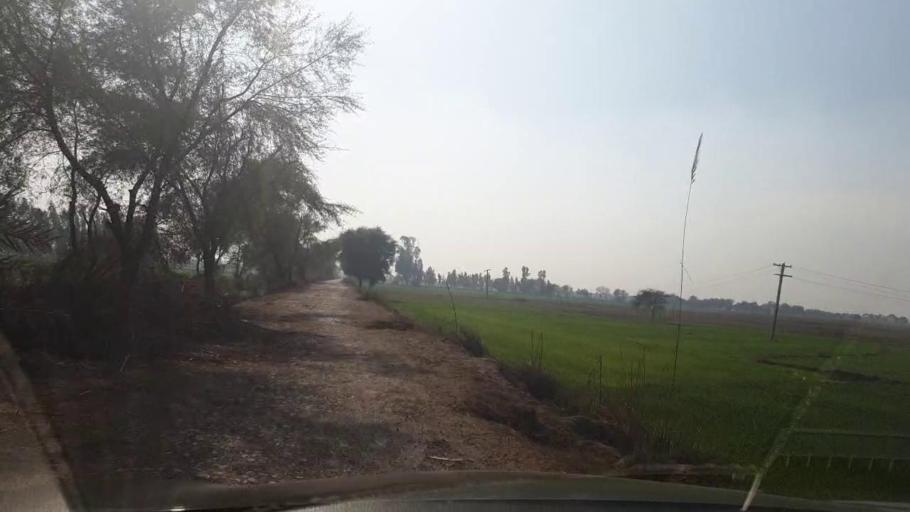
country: PK
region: Sindh
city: Khairpur
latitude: 28.1299
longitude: 69.6459
